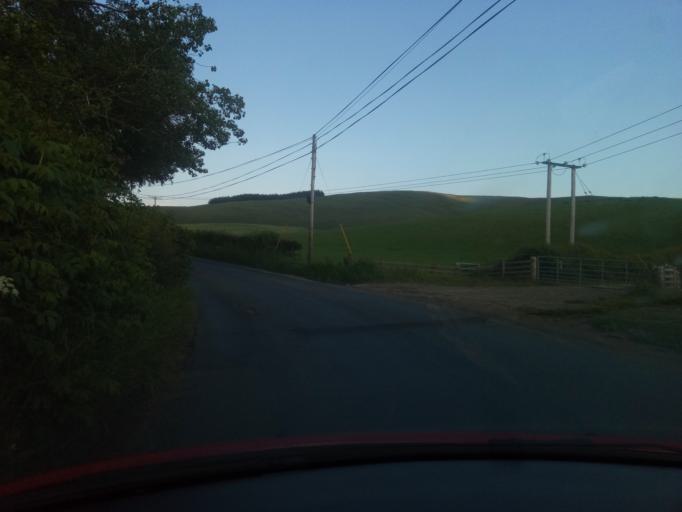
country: GB
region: Scotland
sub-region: The Scottish Borders
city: Selkirk
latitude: 55.5109
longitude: -2.9403
